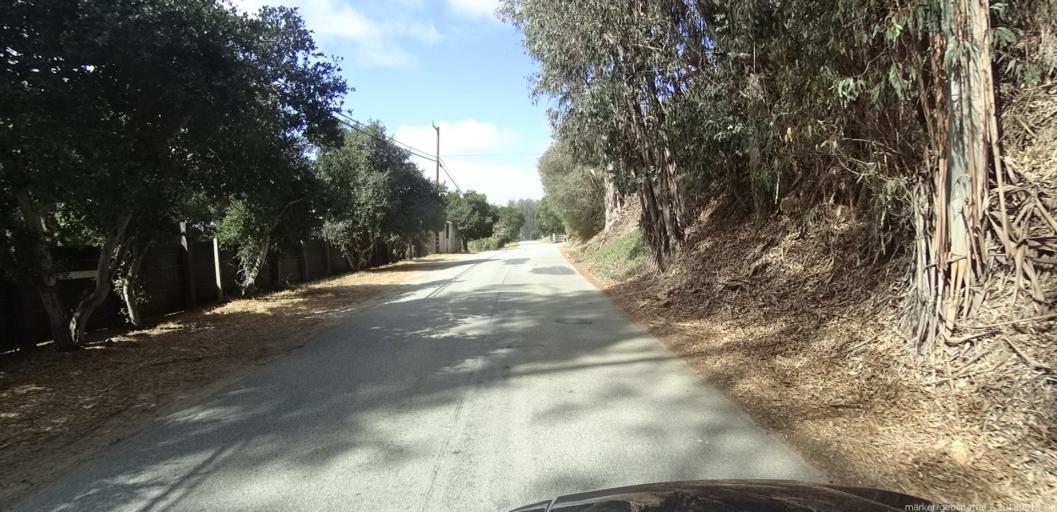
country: US
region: California
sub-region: Monterey County
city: Prunedale
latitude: 36.7874
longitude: -121.6644
